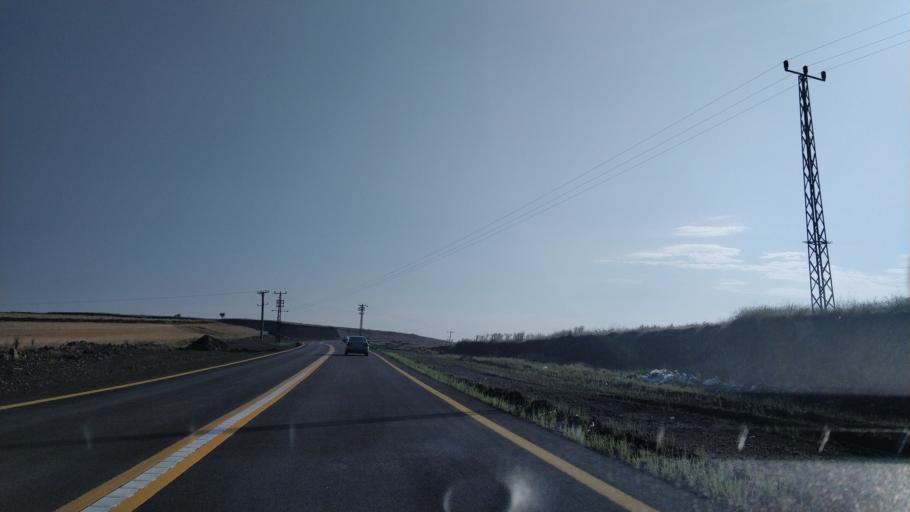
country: TR
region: Ankara
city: Etimesgut
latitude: 39.8597
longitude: 32.5717
